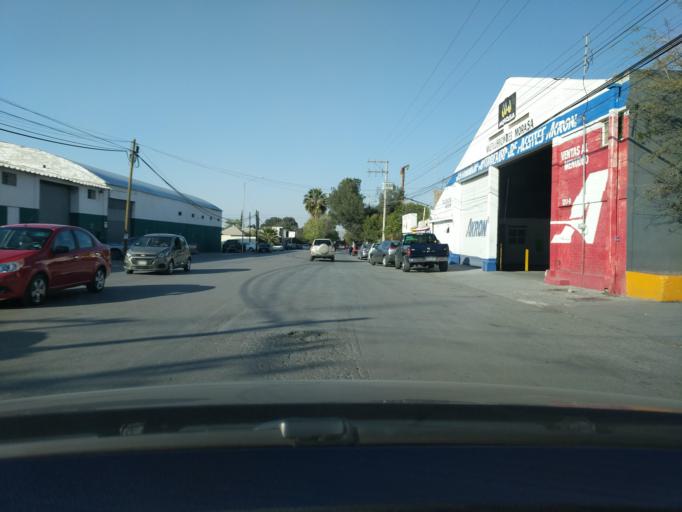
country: MX
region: Coahuila
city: Saltillo
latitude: 25.4674
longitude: -100.9853
